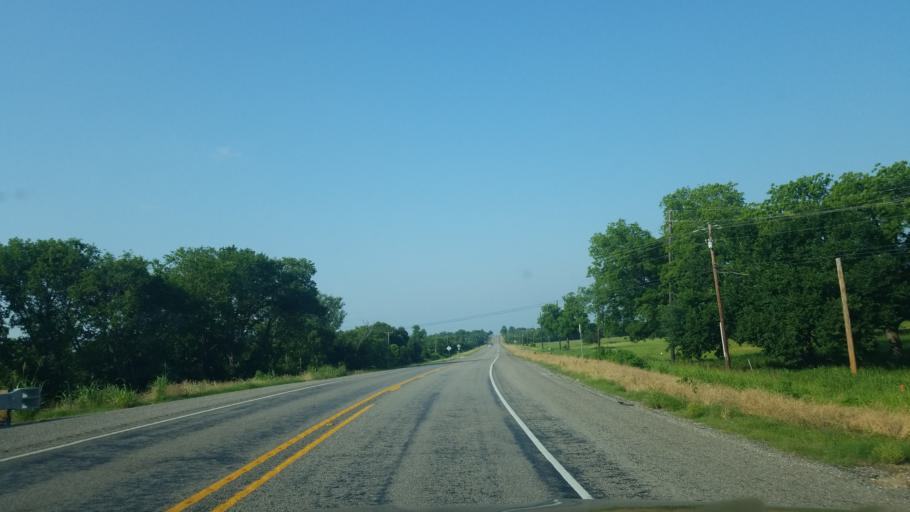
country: US
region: Texas
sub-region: Denton County
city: Denton
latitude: 33.2826
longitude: -97.0920
